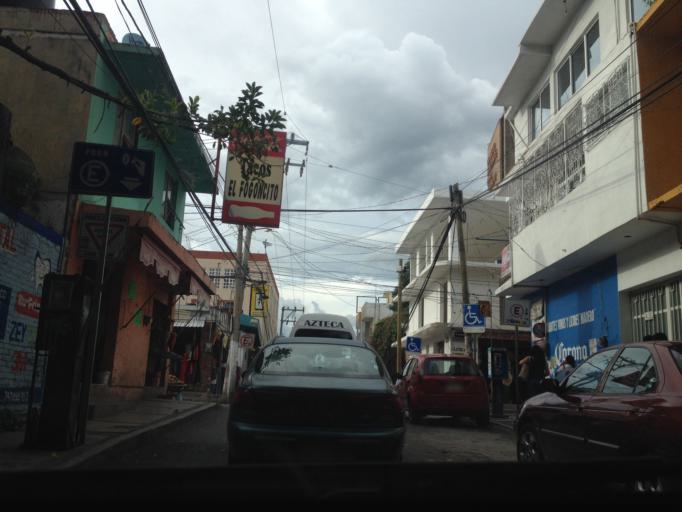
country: MX
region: Guerrero
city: Chilpancingo de los Bravos
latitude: 17.5519
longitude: -99.5029
